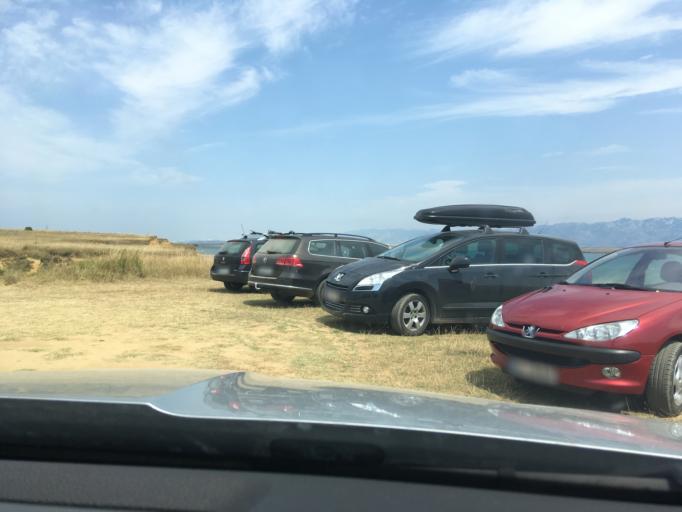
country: HR
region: Zadarska
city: Privlaka
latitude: 44.2687
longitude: 15.1528
